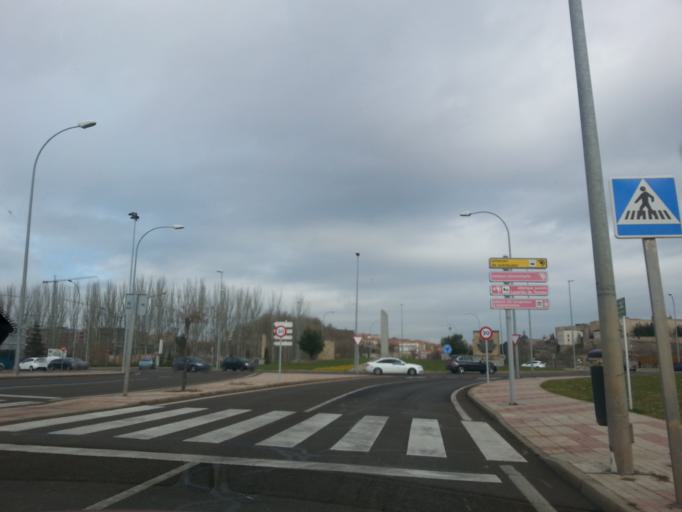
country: ES
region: Castille and Leon
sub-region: Provincia de Salamanca
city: Salamanca
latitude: 40.9572
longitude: -5.6760
